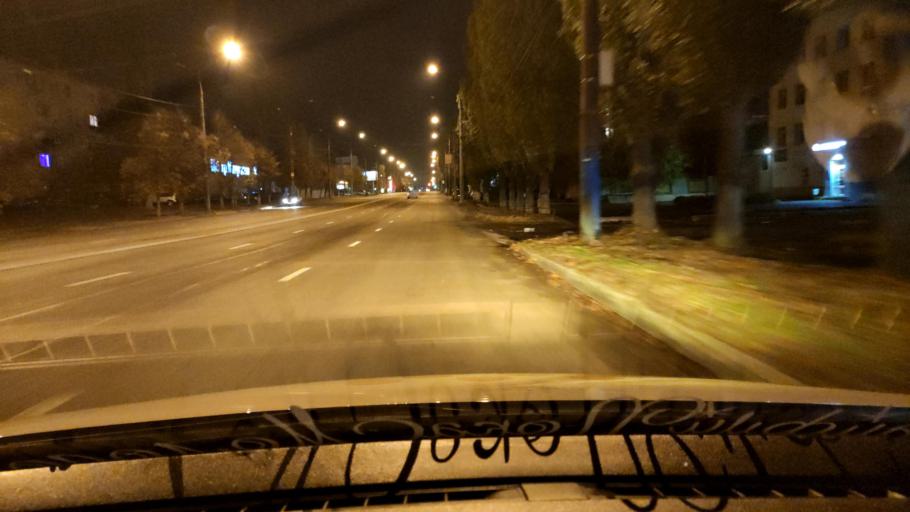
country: RU
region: Voronezj
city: Voronezh
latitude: 51.6827
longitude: 39.1660
